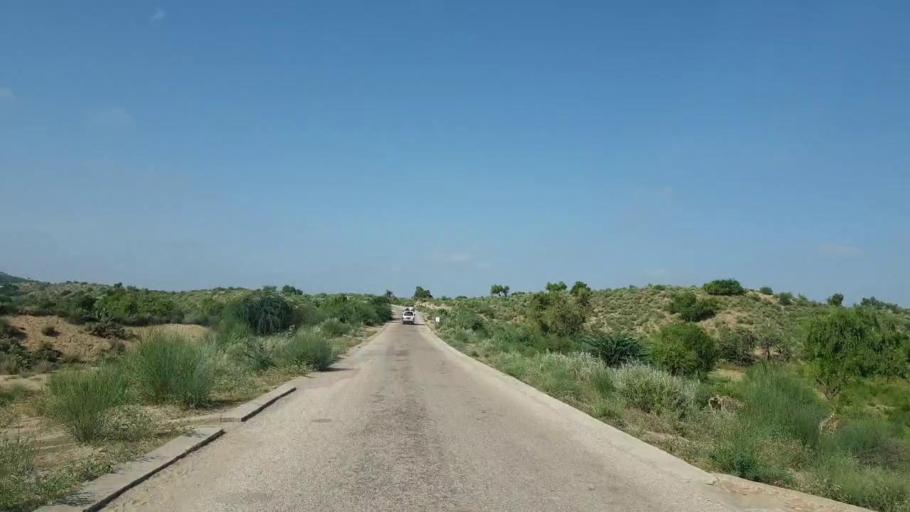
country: PK
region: Sindh
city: Mithi
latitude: 24.5718
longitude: 69.9223
